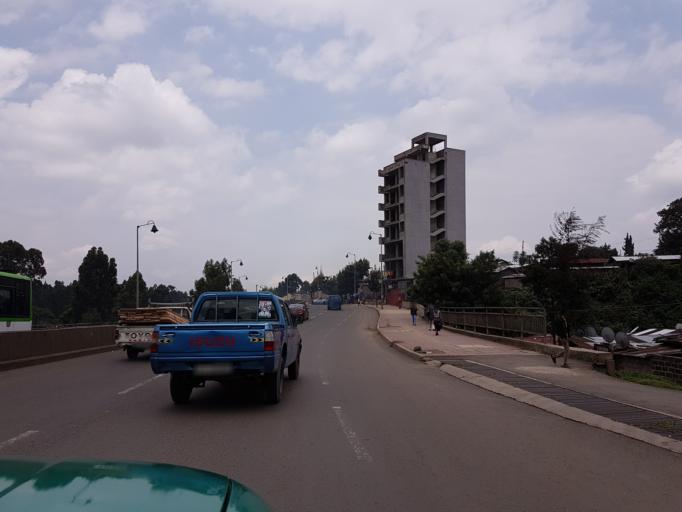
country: ET
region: Adis Abeba
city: Addis Ababa
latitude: 9.0070
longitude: 38.7340
